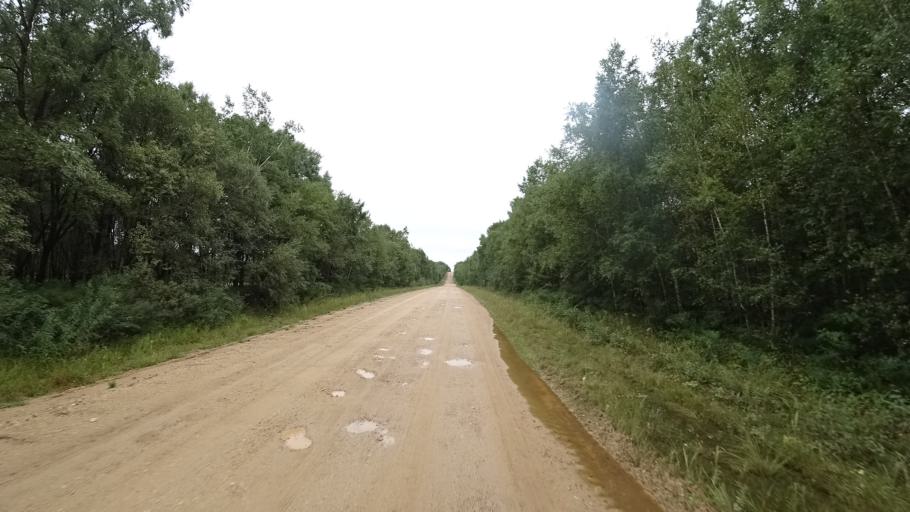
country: RU
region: Primorskiy
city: Ivanovka
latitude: 44.0397
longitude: 132.5384
